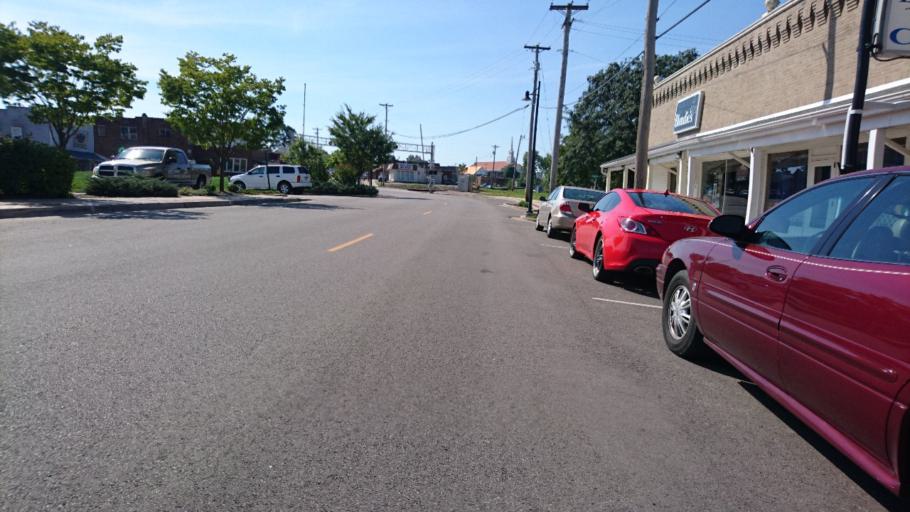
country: US
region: Missouri
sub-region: Franklin County
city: Saint Clair
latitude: 38.3467
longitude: -90.9811
